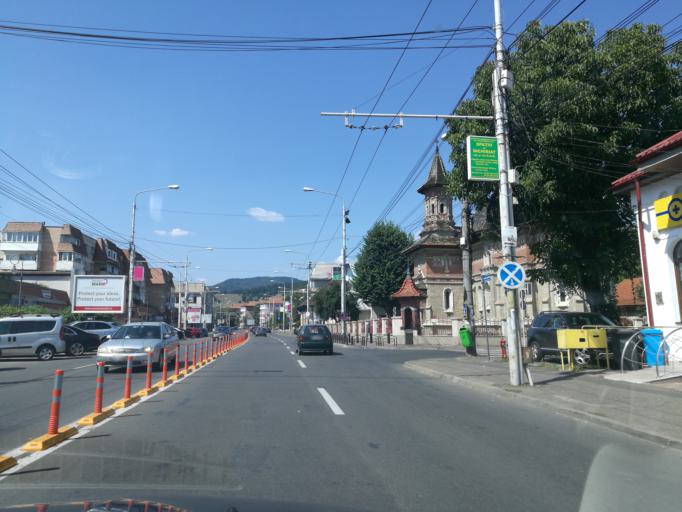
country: RO
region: Neamt
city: Piatra Neamt
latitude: 46.9329
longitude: 26.3607
